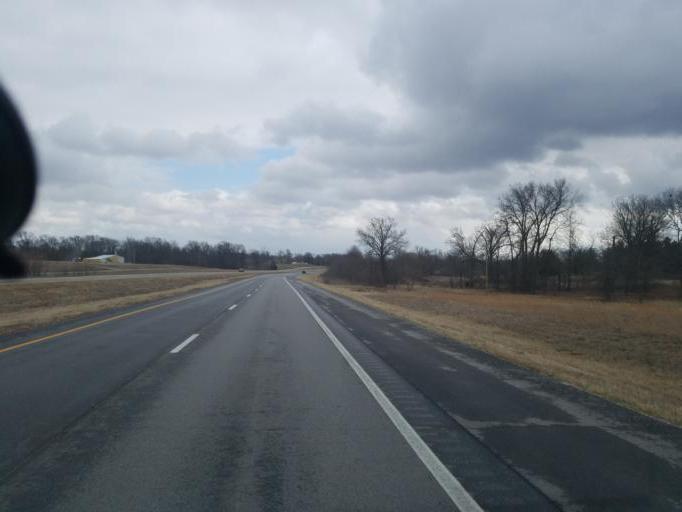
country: US
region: Missouri
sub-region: Randolph County
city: Moberly
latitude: 39.2664
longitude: -92.3389
